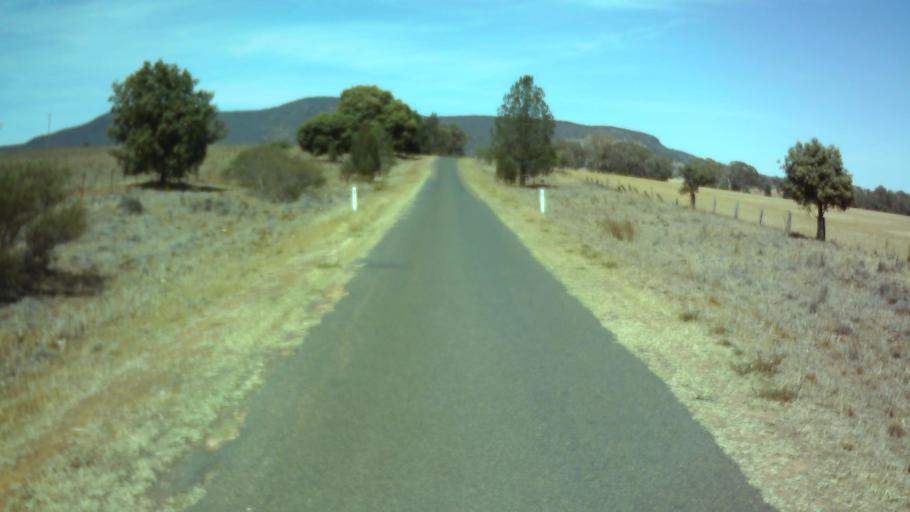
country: AU
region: New South Wales
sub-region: Weddin
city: Grenfell
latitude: -33.8640
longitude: 148.0109
